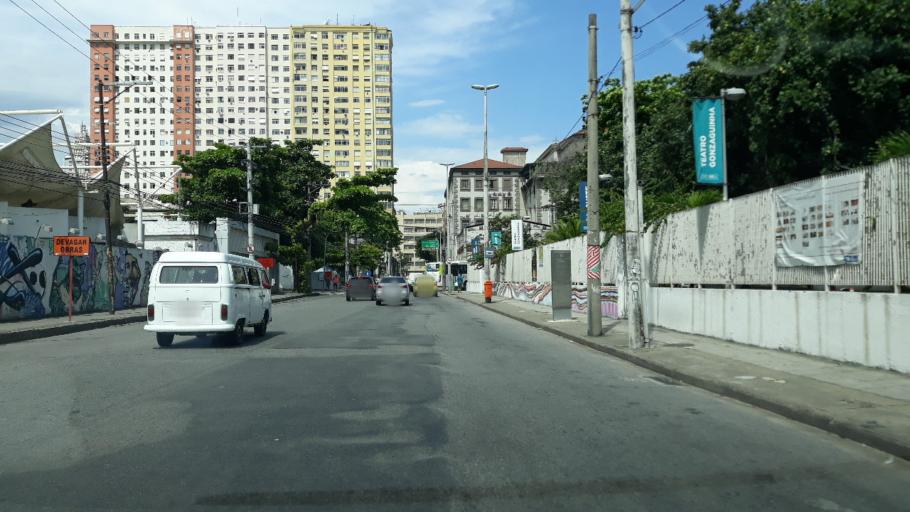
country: BR
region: Rio de Janeiro
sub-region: Rio De Janeiro
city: Rio de Janeiro
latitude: -22.9080
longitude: -43.1961
